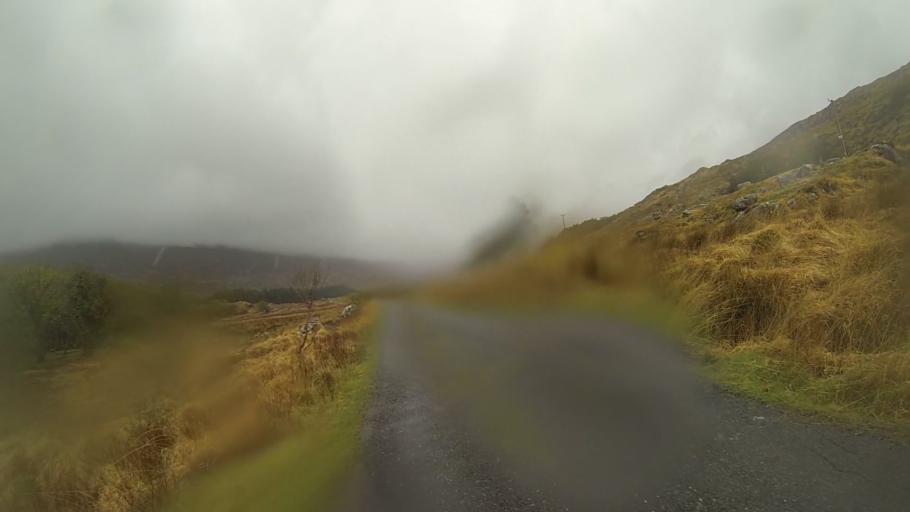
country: IE
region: Munster
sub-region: Ciarrai
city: Kenmare
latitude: 51.9569
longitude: -9.6358
